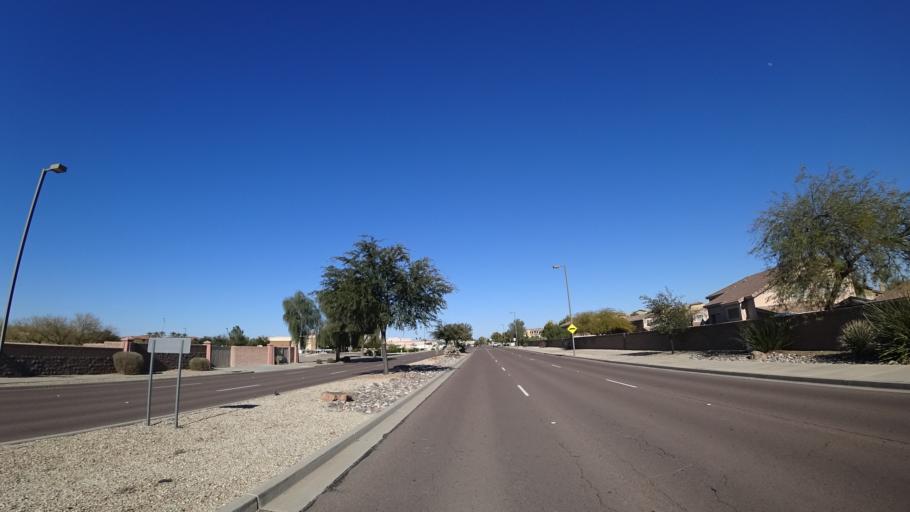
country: US
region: Arizona
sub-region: Maricopa County
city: Sun City West
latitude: 33.6518
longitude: -112.3782
